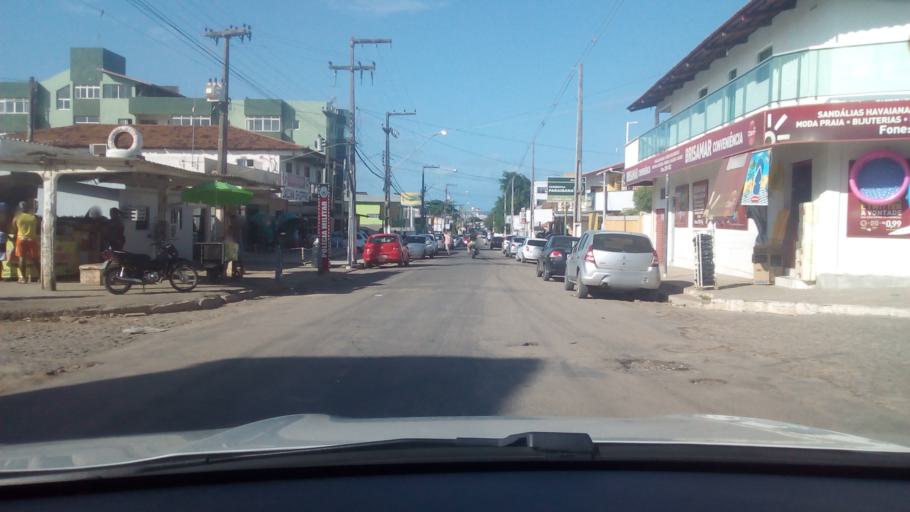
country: BR
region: Paraiba
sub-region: Conde
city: Conde
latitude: -7.2852
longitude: -34.8021
